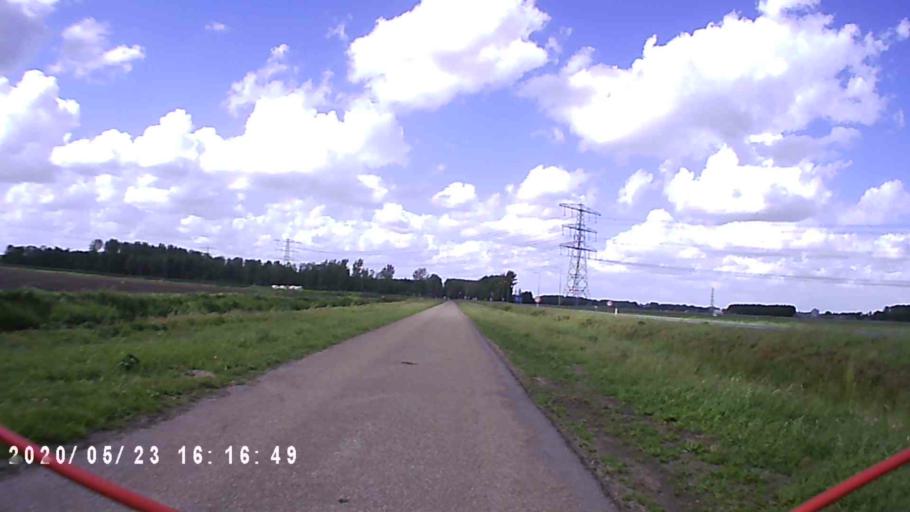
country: NL
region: Groningen
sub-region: Gemeente Appingedam
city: Appingedam
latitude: 53.2637
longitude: 6.8750
